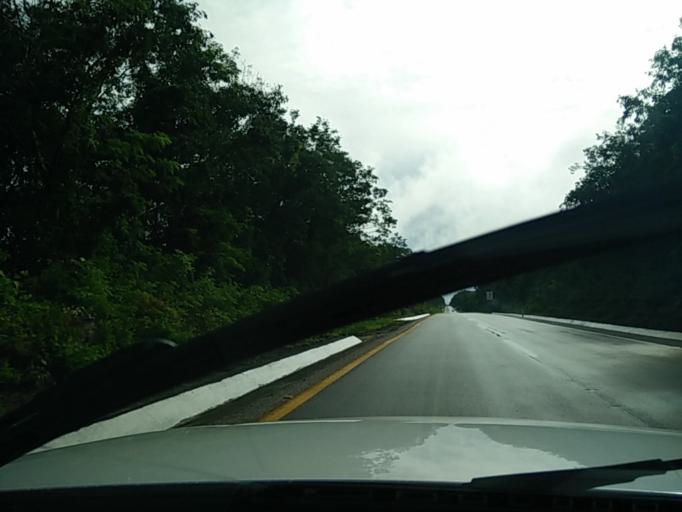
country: MX
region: Yucatan
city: Tunkas
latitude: 20.7592
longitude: -88.7691
